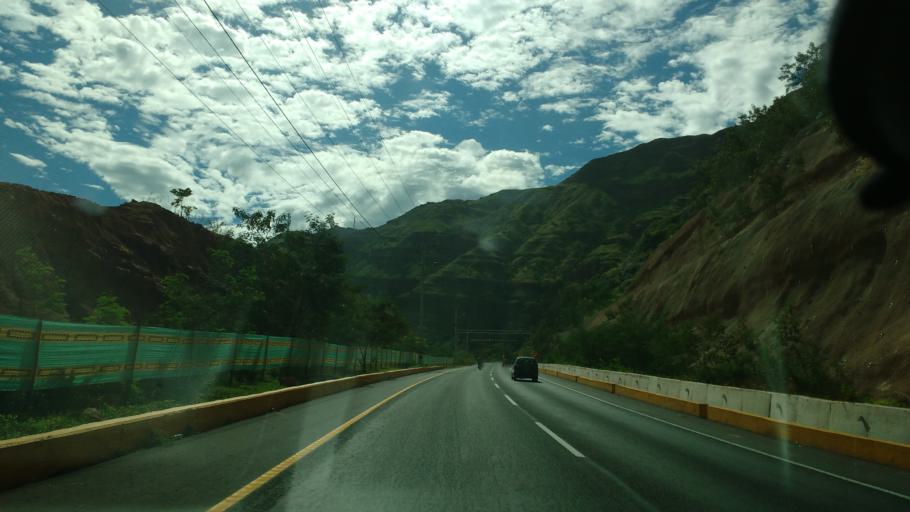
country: CO
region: Tolima
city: Valle de San Juan
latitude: 4.2827
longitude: -75.0196
